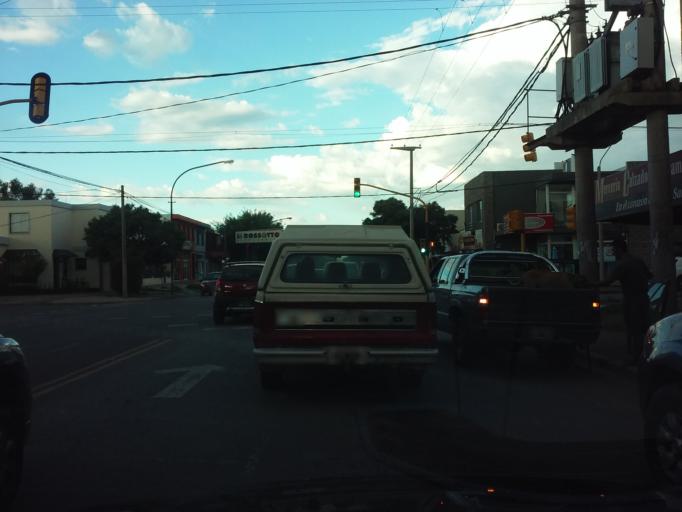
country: AR
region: La Pampa
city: Santa Rosa
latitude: -36.6302
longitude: -64.2936
